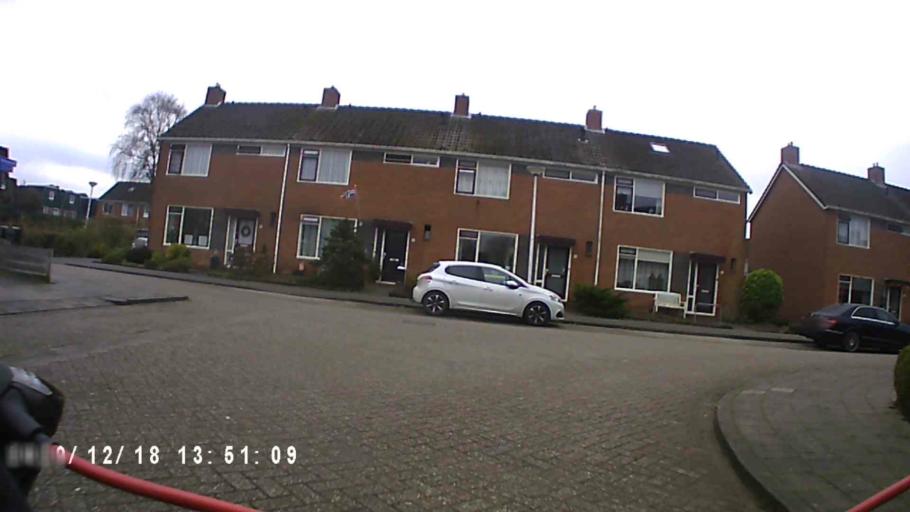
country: NL
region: Groningen
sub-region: Gemeente Bedum
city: Bedum
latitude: 53.2983
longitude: 6.6086
